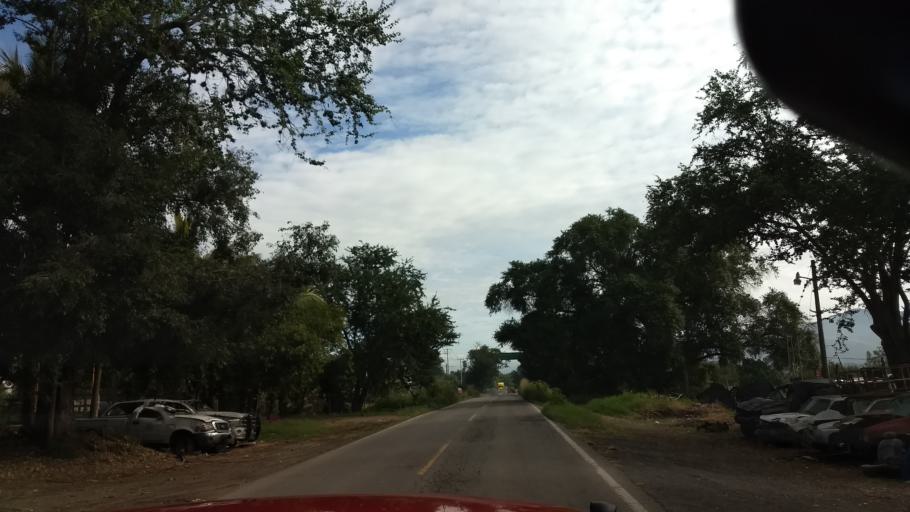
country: MX
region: Jalisco
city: Tuxpan
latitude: 19.5470
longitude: -103.3980
